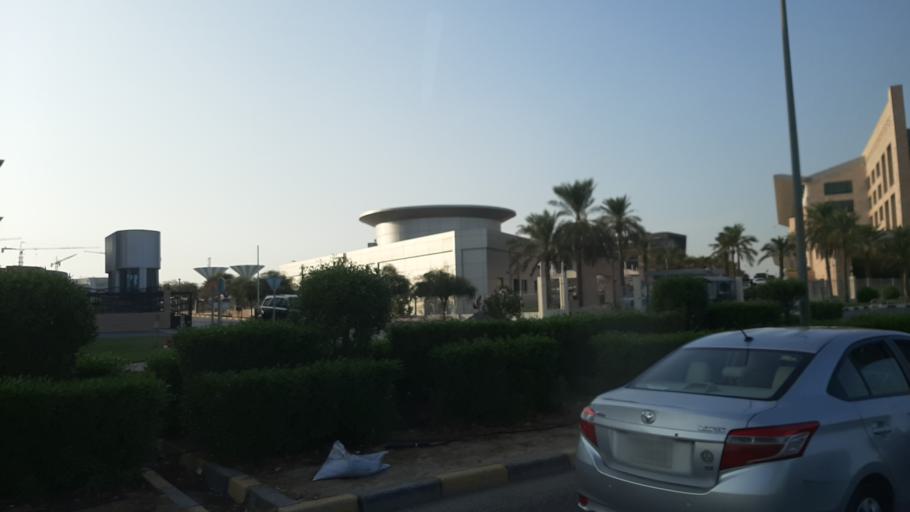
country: KW
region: Al Ahmadi
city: Al Ahmadi
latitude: 29.0911
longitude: 48.0882
